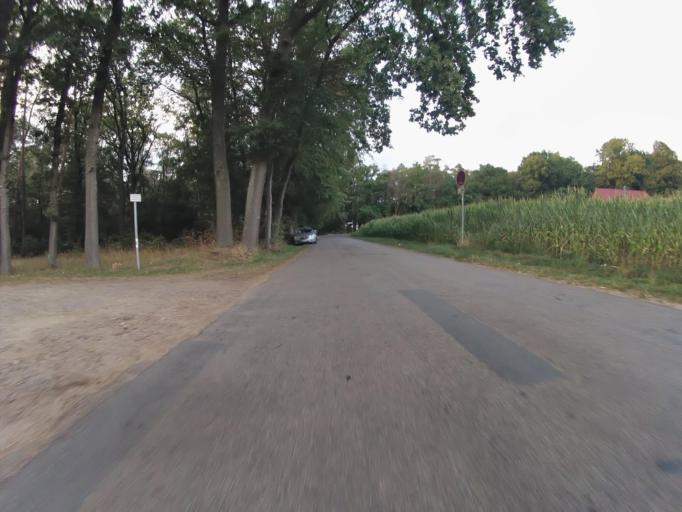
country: DE
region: North Rhine-Westphalia
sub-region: Regierungsbezirk Munster
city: Westerkappeln
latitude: 52.3297
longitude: 7.9103
